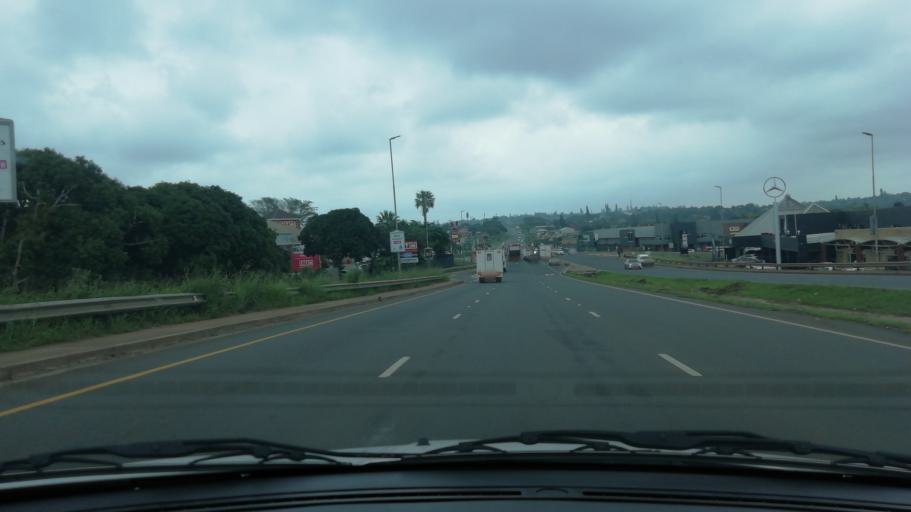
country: ZA
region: KwaZulu-Natal
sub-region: uThungulu District Municipality
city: Empangeni
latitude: -28.7664
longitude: 31.9104
